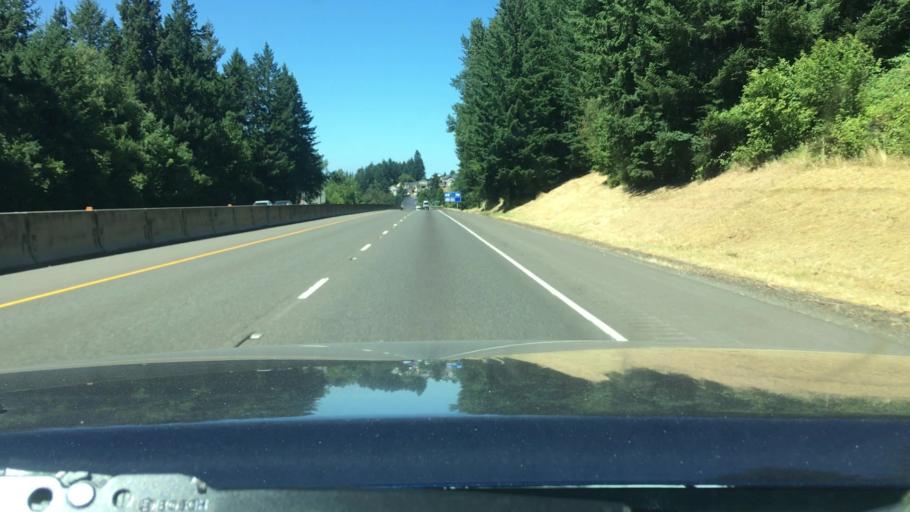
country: US
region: Oregon
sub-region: Lane County
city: Cottage Grove
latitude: 43.7833
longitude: -123.0552
